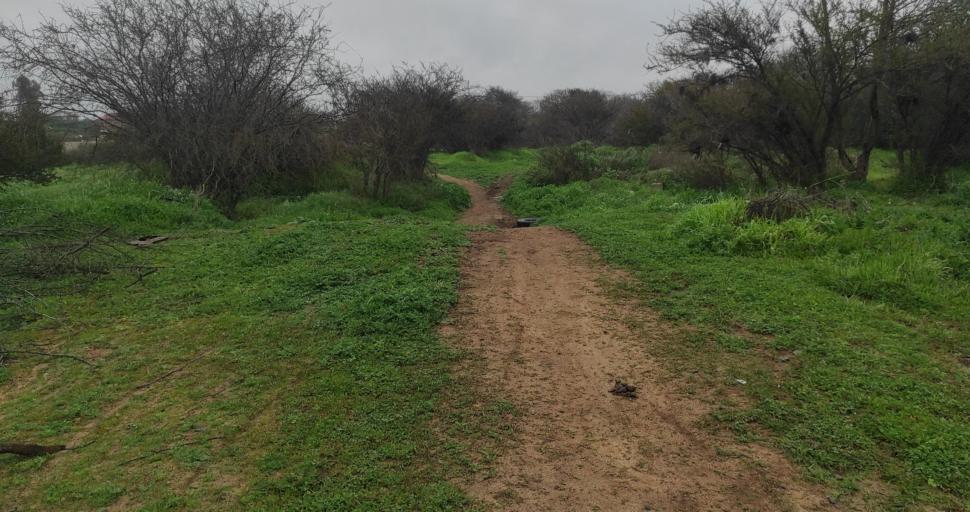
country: CL
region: Valparaiso
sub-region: Provincia de Marga Marga
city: Limache
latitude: -33.0212
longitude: -71.2600
